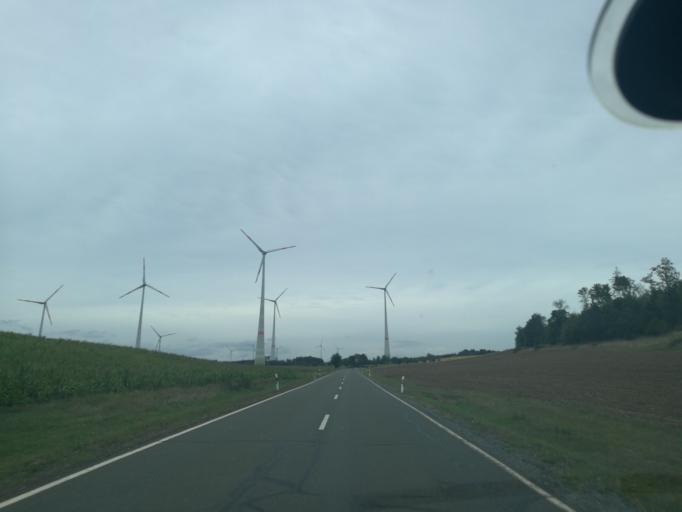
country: DE
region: Bavaria
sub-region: Upper Franconia
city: Gattendorf
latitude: 50.2988
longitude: 12.0121
